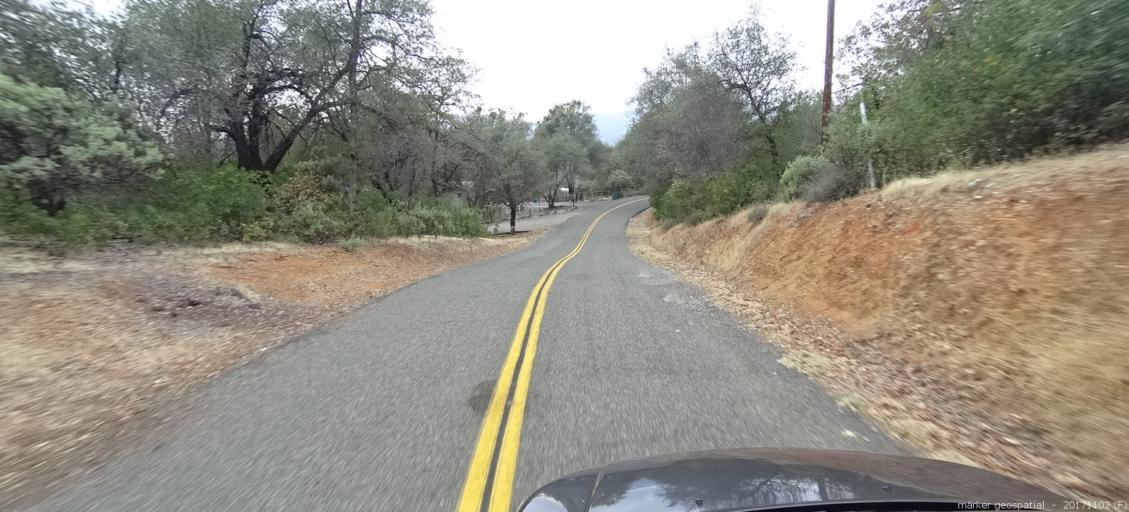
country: US
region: California
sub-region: Shasta County
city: Central Valley (historical)
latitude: 40.6564
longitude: -122.4254
